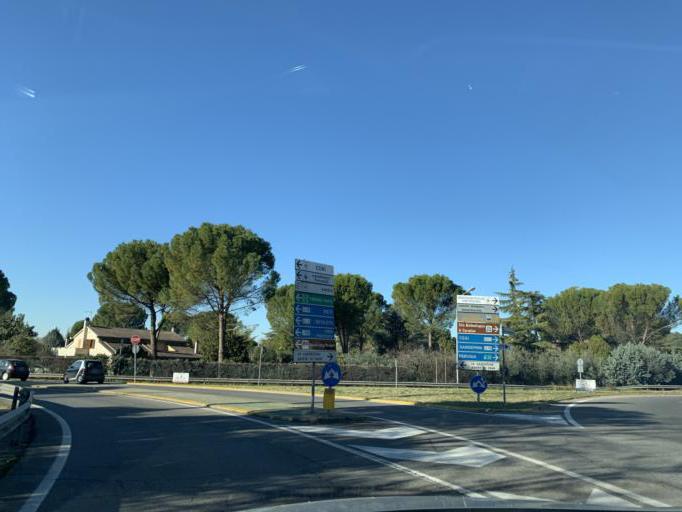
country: IT
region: Umbria
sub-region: Provincia di Terni
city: Terni
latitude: 42.5763
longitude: 12.6260
